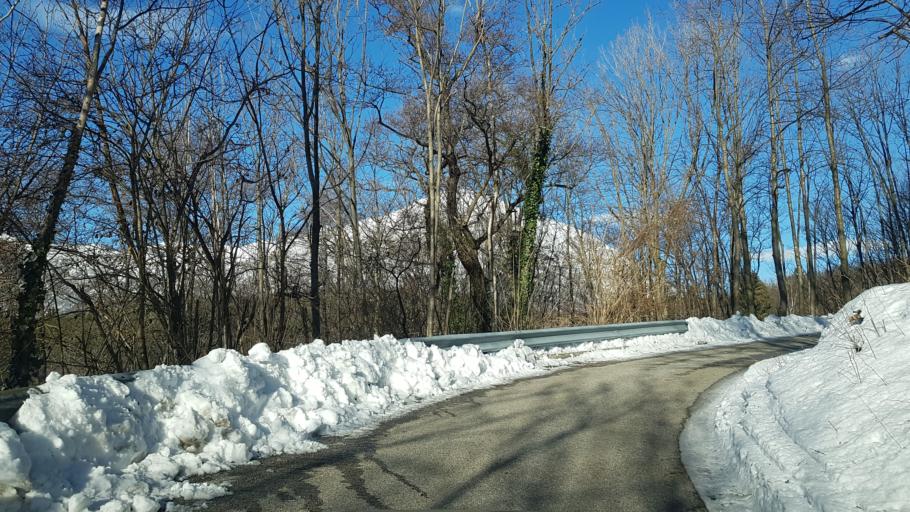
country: IT
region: Friuli Venezia Giulia
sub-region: Provincia di Udine
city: Forgaria nel Friuli
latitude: 46.2500
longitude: 12.9906
